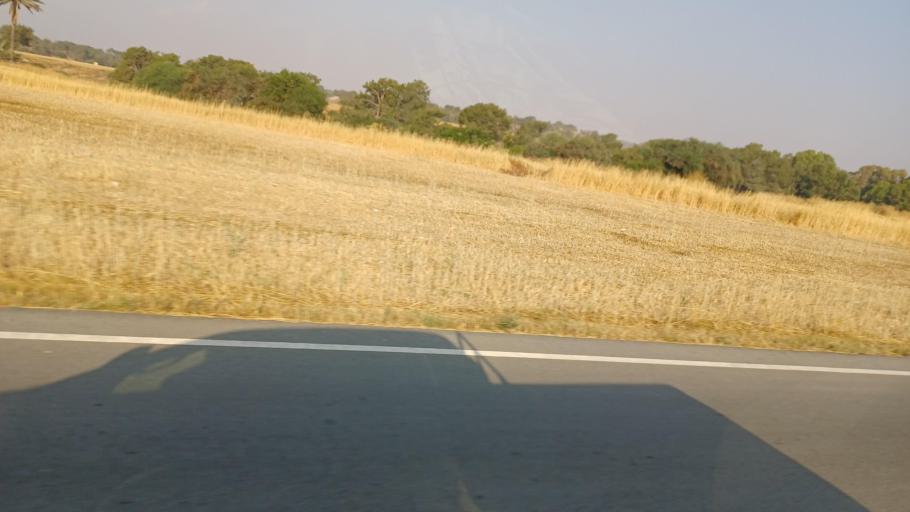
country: CY
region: Larnaka
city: Tersefanou
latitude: 34.8307
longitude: 33.5099
